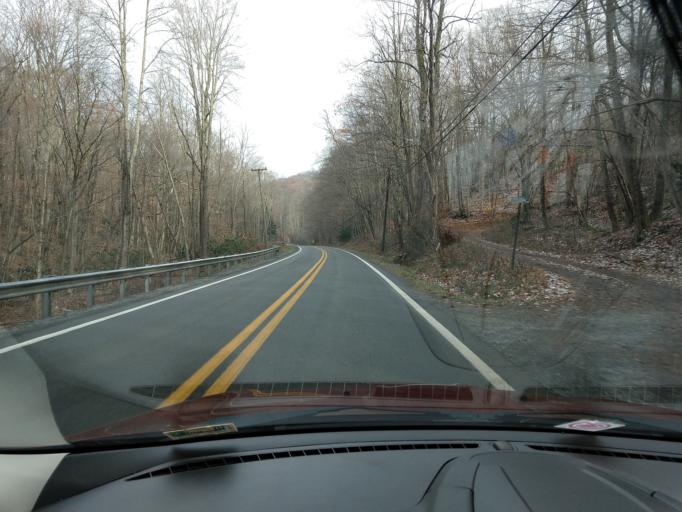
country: US
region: West Virginia
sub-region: Greenbrier County
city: Rainelle
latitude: 38.0692
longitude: -80.7072
